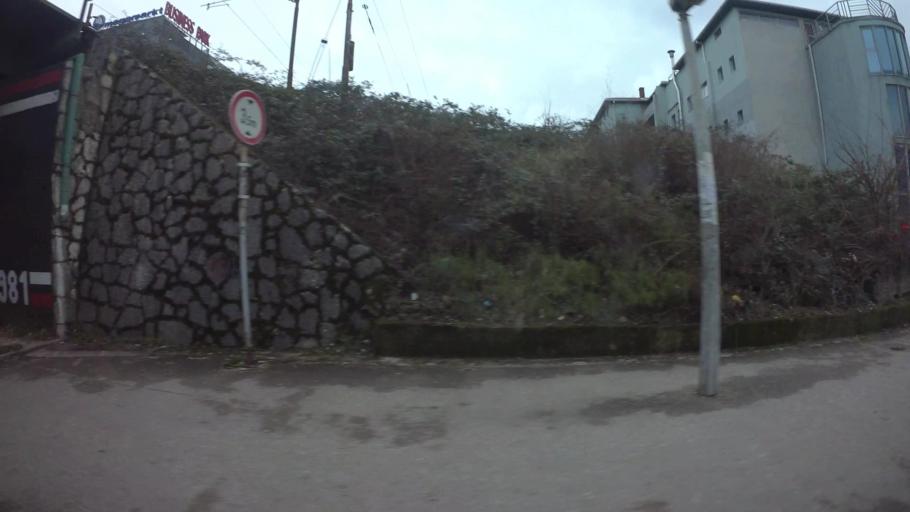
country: BA
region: Federation of Bosnia and Herzegovina
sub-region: Hercegovacko-Bosanski Kanton
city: Mostar
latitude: 43.3556
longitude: 17.8130
